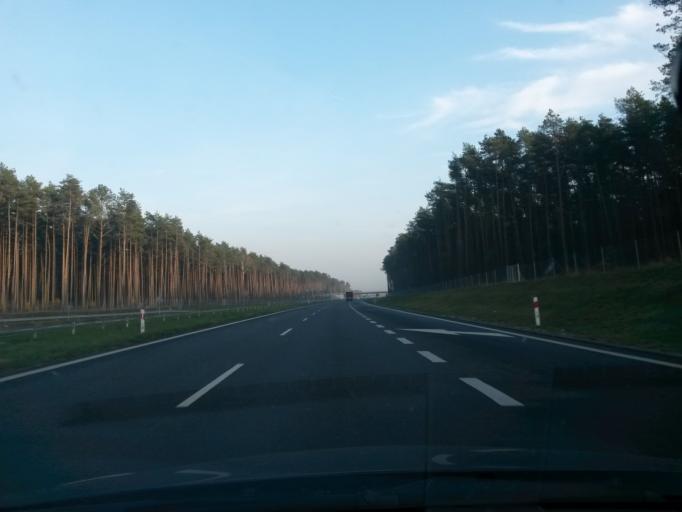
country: PL
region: Greater Poland Voivodeship
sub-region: Powiat kepinski
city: Bralin
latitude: 51.3001
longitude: 17.8745
